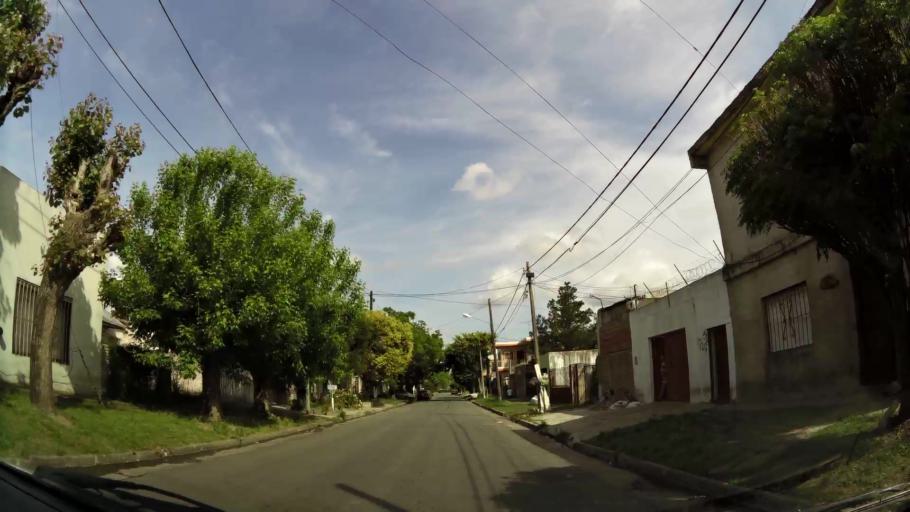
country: AR
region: Buenos Aires
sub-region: Partido de Quilmes
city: Quilmes
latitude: -34.7611
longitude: -58.2365
